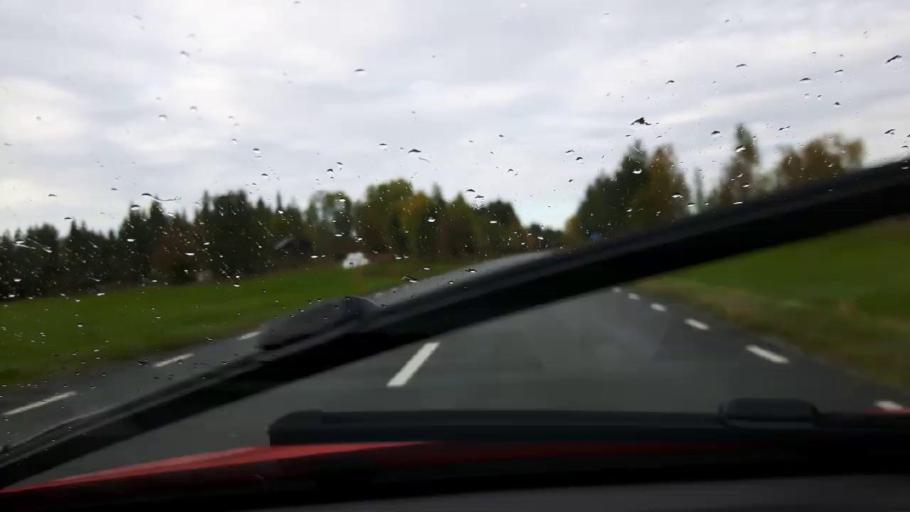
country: SE
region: Jaemtland
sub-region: Krokoms Kommun
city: Krokom
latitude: 63.1044
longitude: 14.2969
